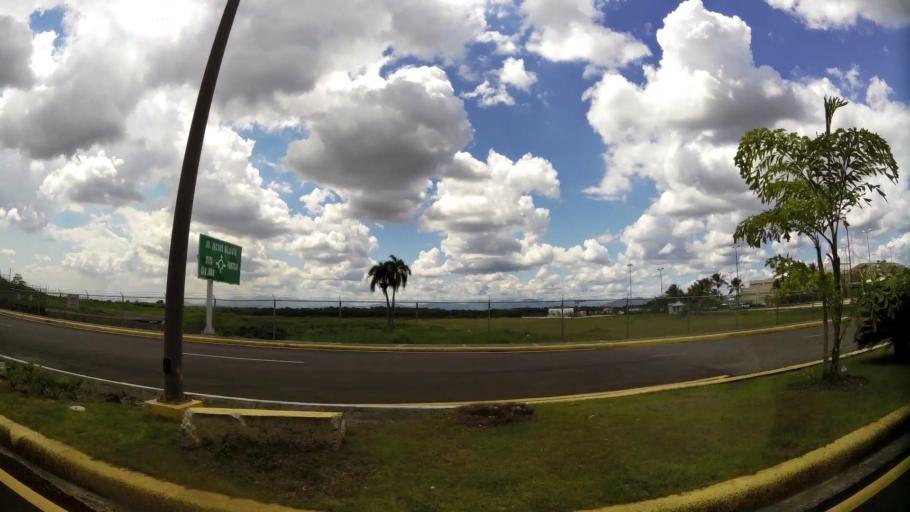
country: DO
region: Nacional
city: Santo Domingo
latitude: 18.5745
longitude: -69.9807
